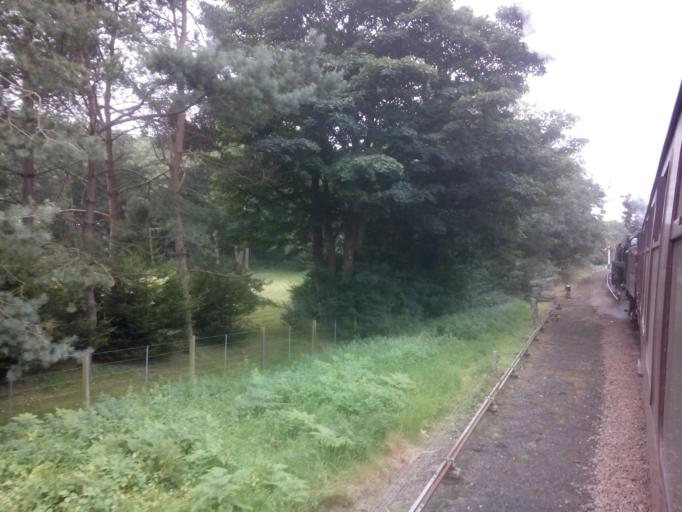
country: GB
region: England
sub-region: Norfolk
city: Sheringham
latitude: 52.9325
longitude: 1.1483
